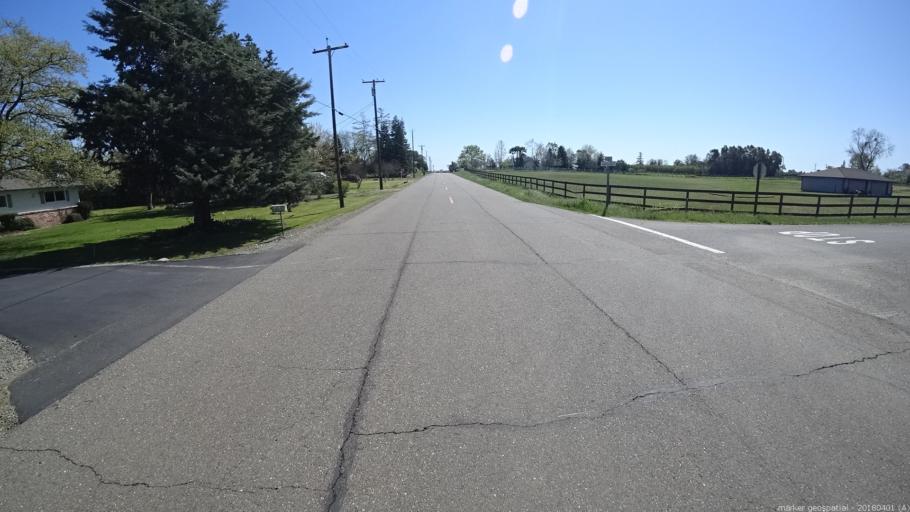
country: US
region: California
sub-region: Sacramento County
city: Wilton
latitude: 38.4161
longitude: -121.2097
